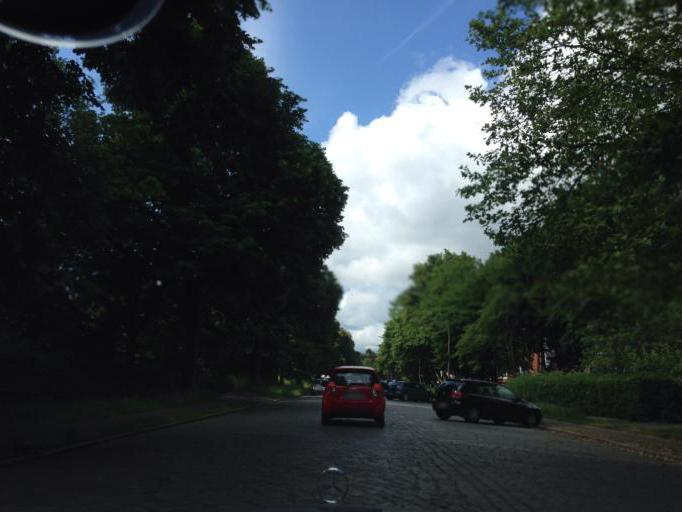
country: DE
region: Hamburg
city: Marienthal
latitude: 53.5859
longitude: 10.0737
